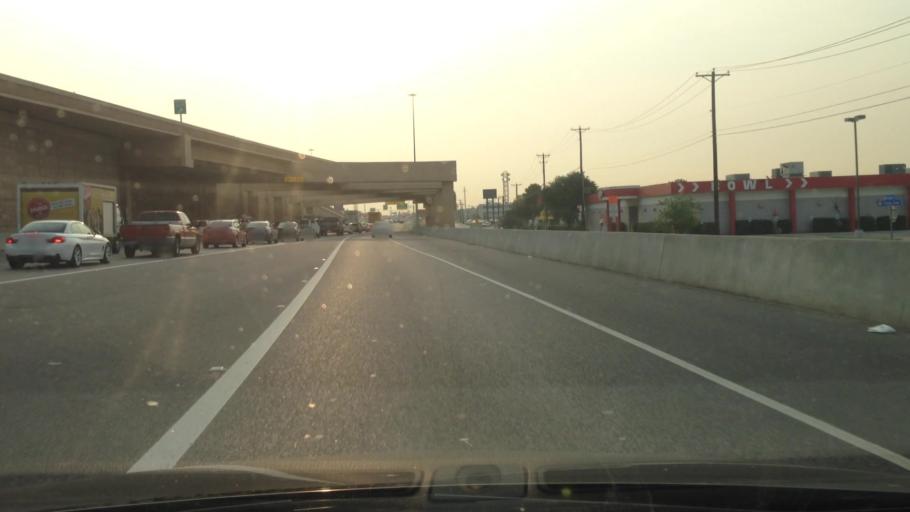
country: US
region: Texas
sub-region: Tarrant County
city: Bedford
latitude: 32.8373
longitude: -97.1147
